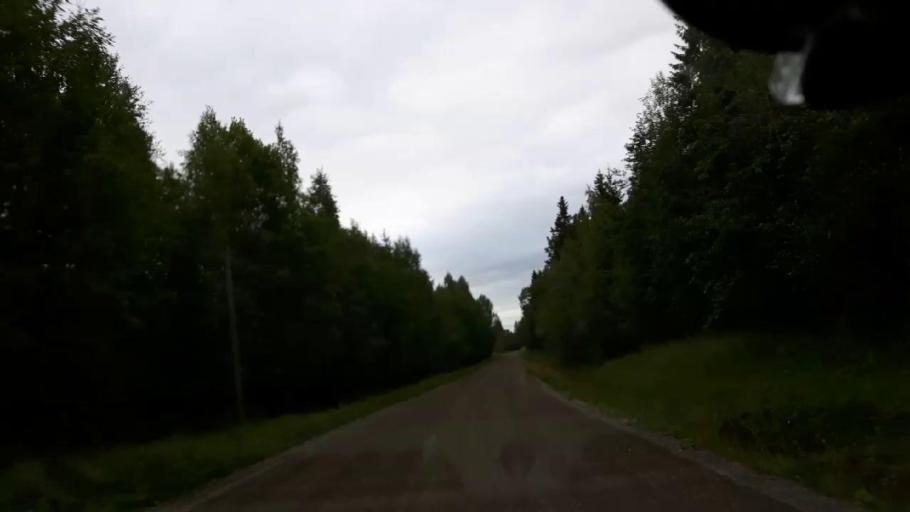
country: SE
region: Jaemtland
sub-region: Braecke Kommun
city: Braecke
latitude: 62.9101
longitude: 15.5890
